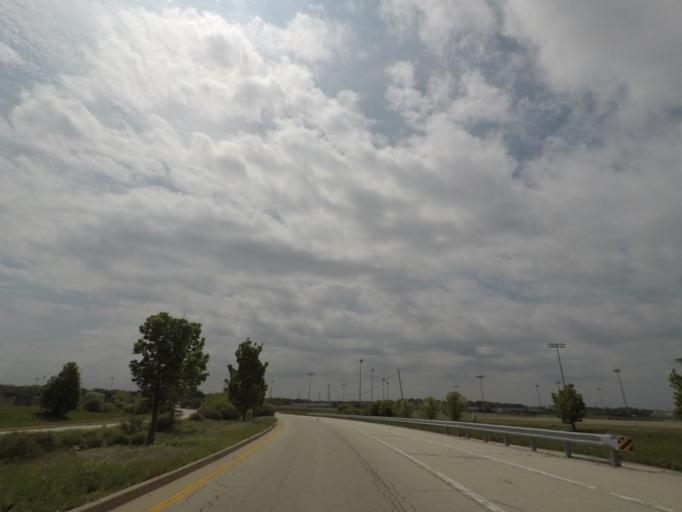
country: US
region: Illinois
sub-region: Winnebago County
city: Cherry Valley
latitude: 42.3245
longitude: -88.9502
